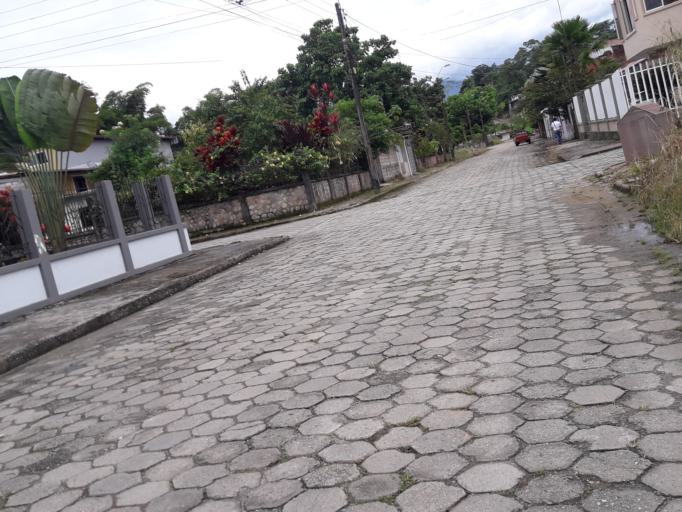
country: EC
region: Napo
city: Tena
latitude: -0.9849
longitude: -77.8159
